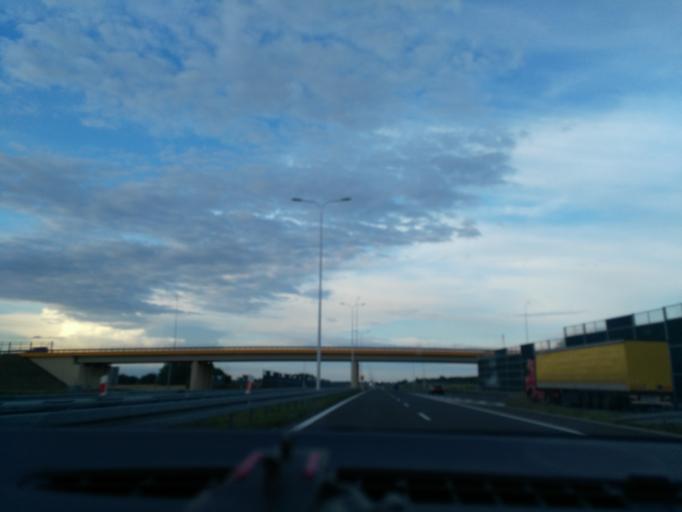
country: PL
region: Lublin Voivodeship
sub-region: Powiat lubelski
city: Jastkow
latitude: 51.2881
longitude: 22.4597
